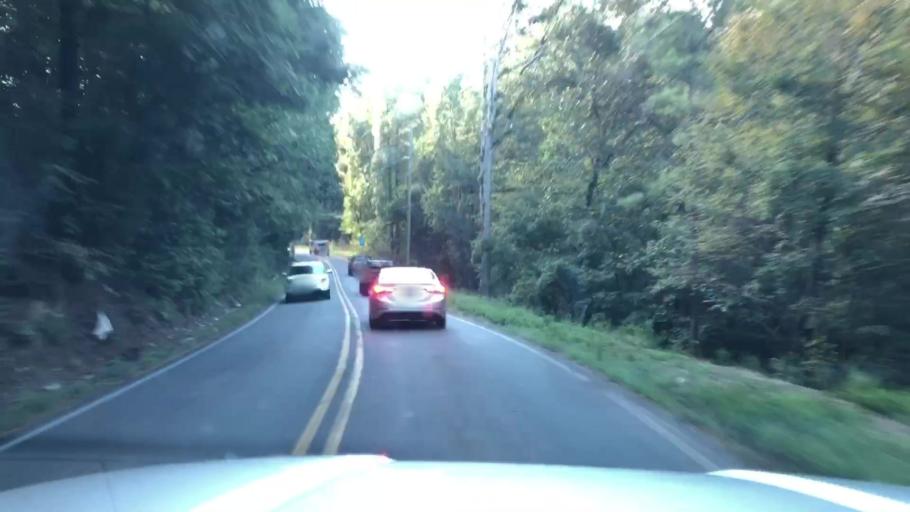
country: US
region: Georgia
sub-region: Bartow County
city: Emerson
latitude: 34.0804
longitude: -84.7342
